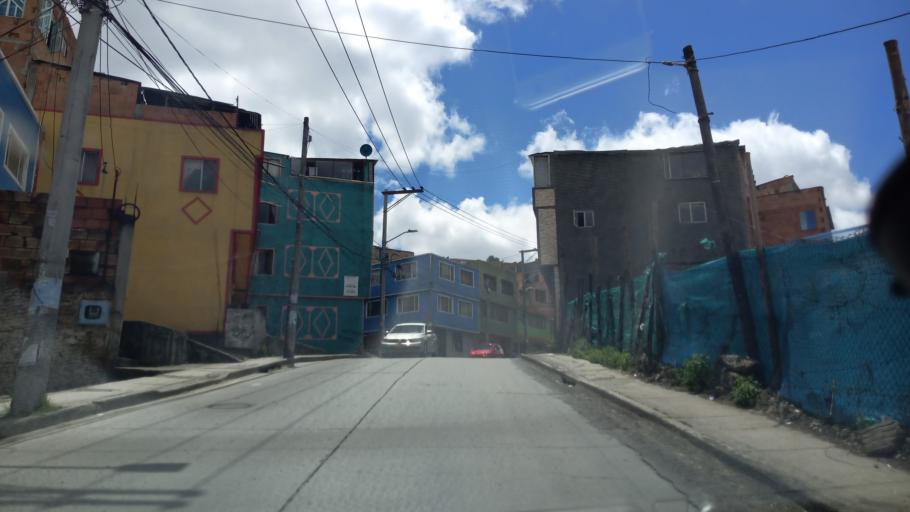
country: CO
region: Bogota D.C.
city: Bogota
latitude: 4.5660
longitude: -74.1121
